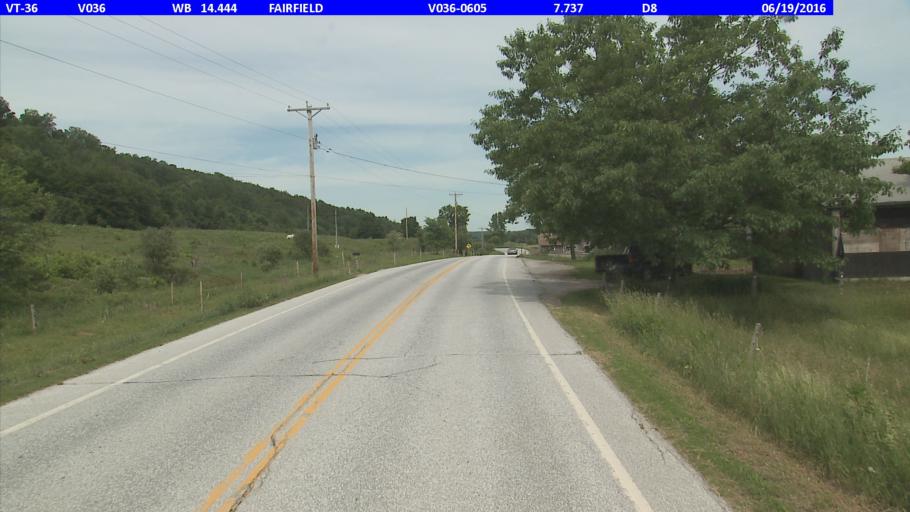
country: US
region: Vermont
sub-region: Franklin County
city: Enosburg Falls
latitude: 44.7974
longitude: -72.8870
